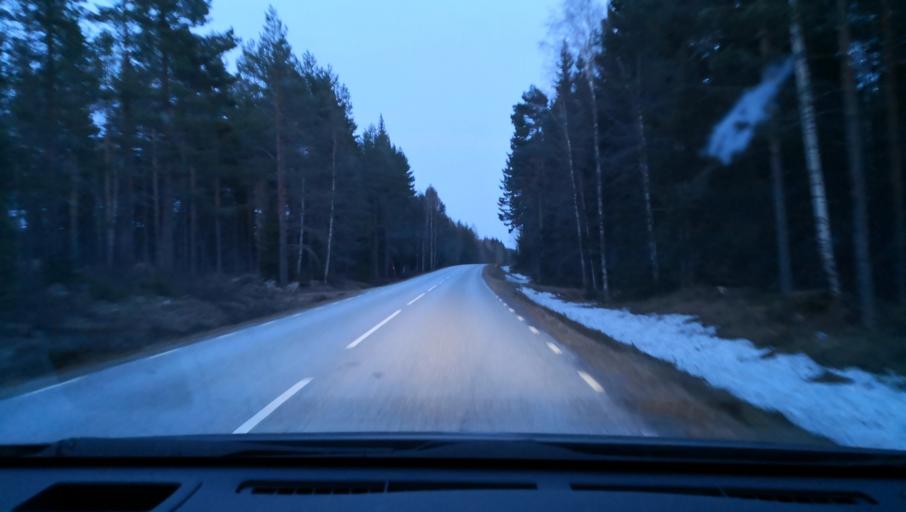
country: SE
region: OErebro
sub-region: Lindesbergs Kommun
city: Frovi
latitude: 59.5952
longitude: 15.3842
